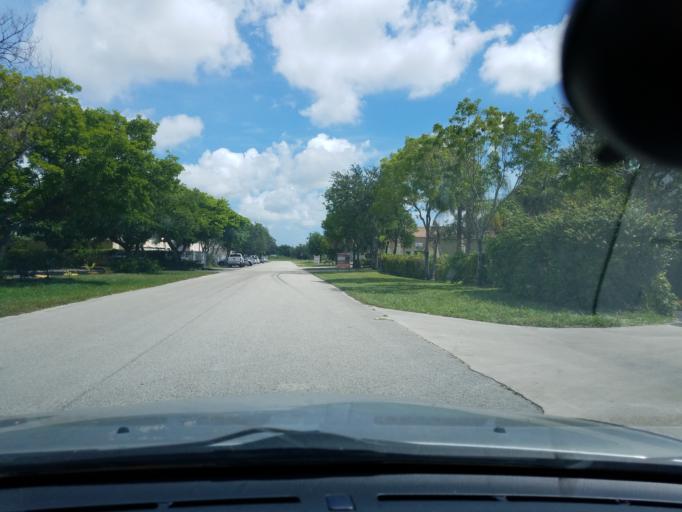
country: US
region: Florida
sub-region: Palm Beach County
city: North Palm Beach
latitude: 26.7983
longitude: -80.0927
